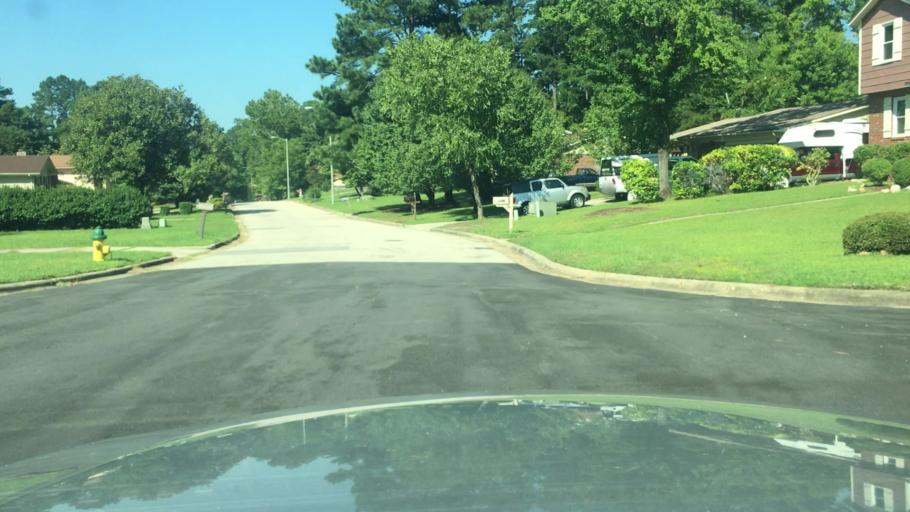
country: US
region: North Carolina
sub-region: Cumberland County
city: Fayetteville
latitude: 35.1090
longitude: -78.9033
